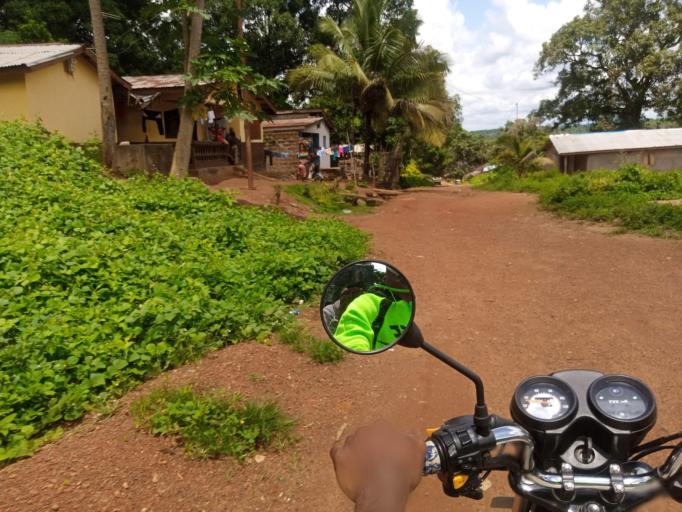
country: SL
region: Northern Province
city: Port Loko
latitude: 8.7629
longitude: -12.7887
